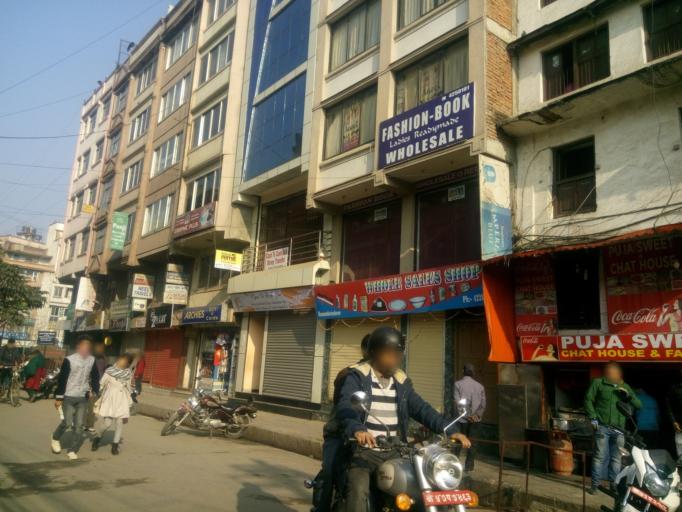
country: NP
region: Central Region
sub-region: Bagmati Zone
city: Kathmandu
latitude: 27.7015
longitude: 85.3094
